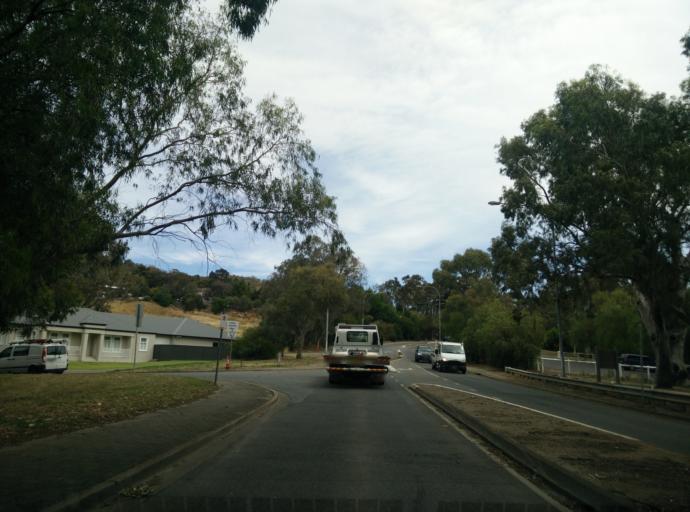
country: AU
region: South Australia
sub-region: Mitcham
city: Mitcham
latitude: -34.9809
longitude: 138.6222
